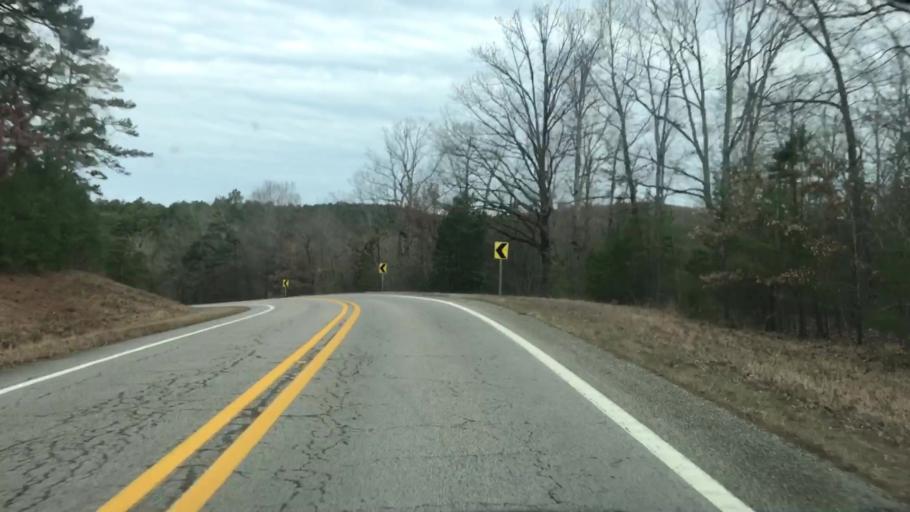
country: US
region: Arkansas
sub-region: Montgomery County
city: Mount Ida
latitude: 34.6686
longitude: -93.7756
